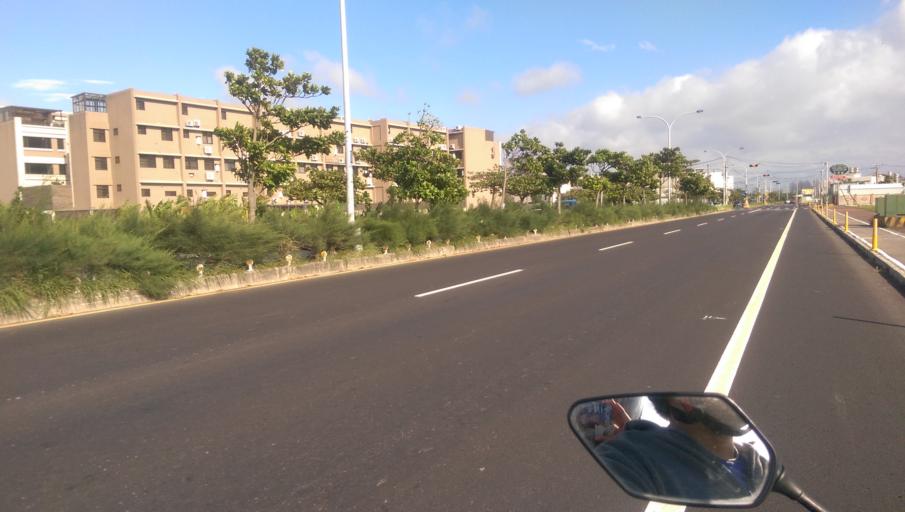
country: TW
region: Taiwan
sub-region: Hsinchu
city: Hsinchu
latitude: 24.8354
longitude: 120.9411
